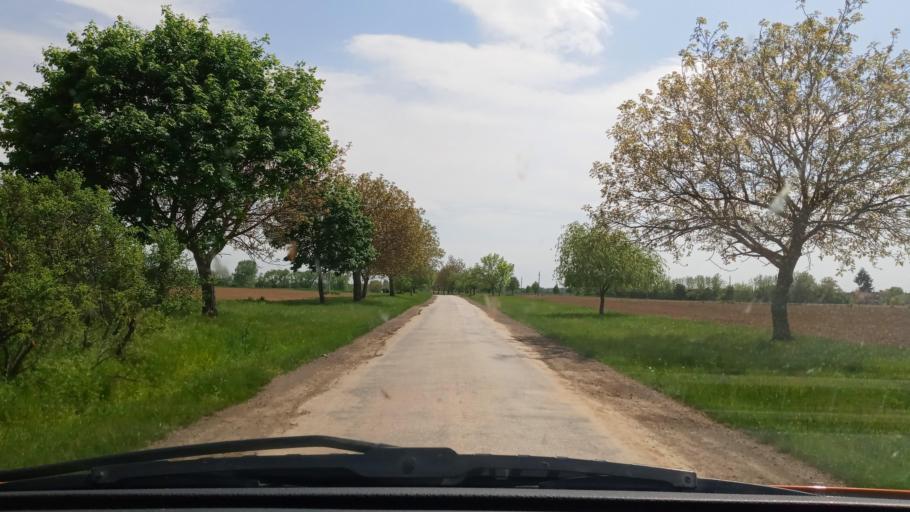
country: HU
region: Baranya
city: Villany
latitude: 45.8239
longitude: 18.5045
